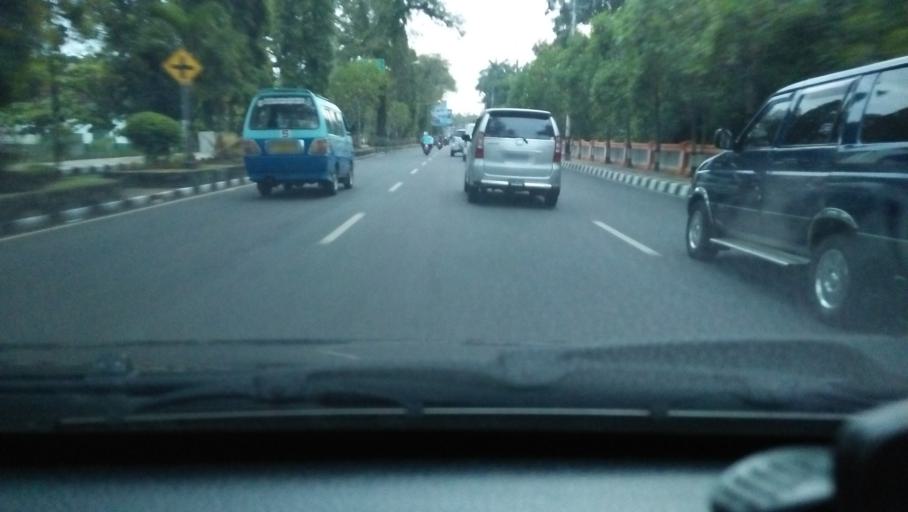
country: ID
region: Central Java
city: Magelang
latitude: -7.4674
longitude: 110.2204
